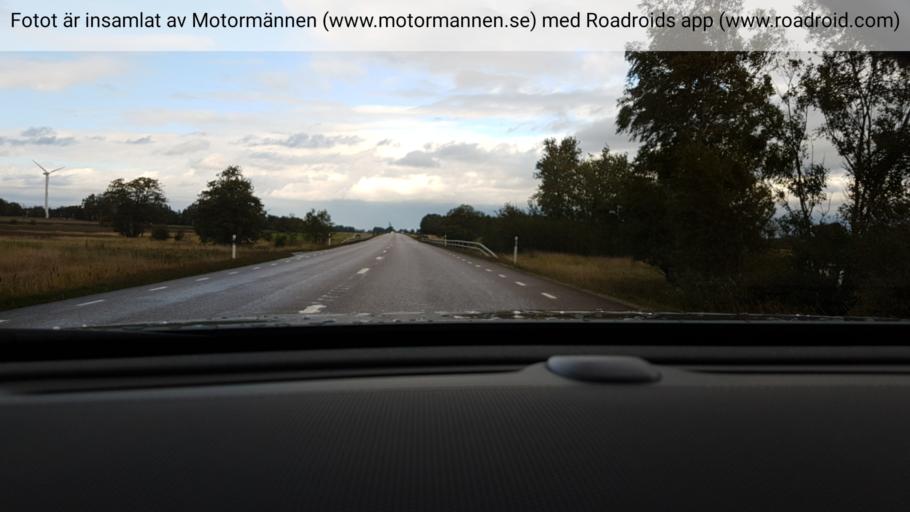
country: SE
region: Vaestra Goetaland
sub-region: Vanersborgs Kommun
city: Bralanda
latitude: 58.5279
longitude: 12.3153
